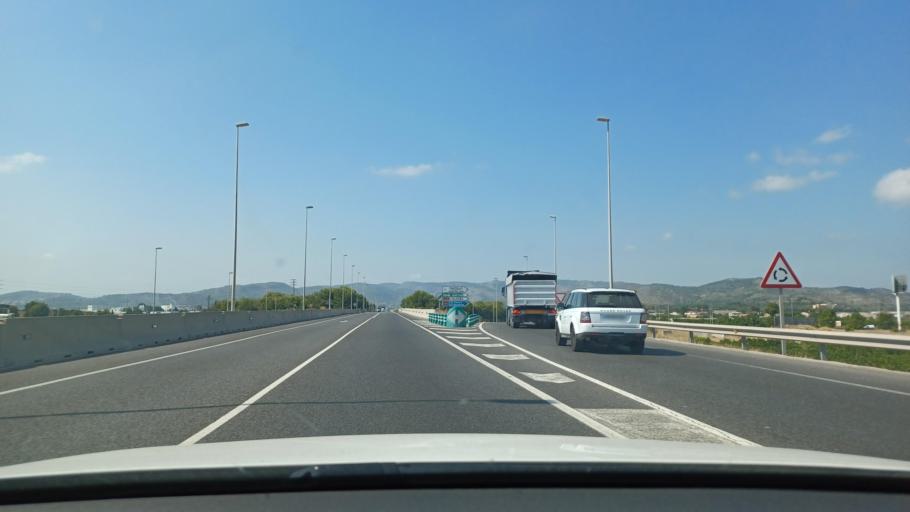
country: ES
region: Valencia
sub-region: Provincia de Castello
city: Almassora
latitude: 39.9810
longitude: -0.0876
